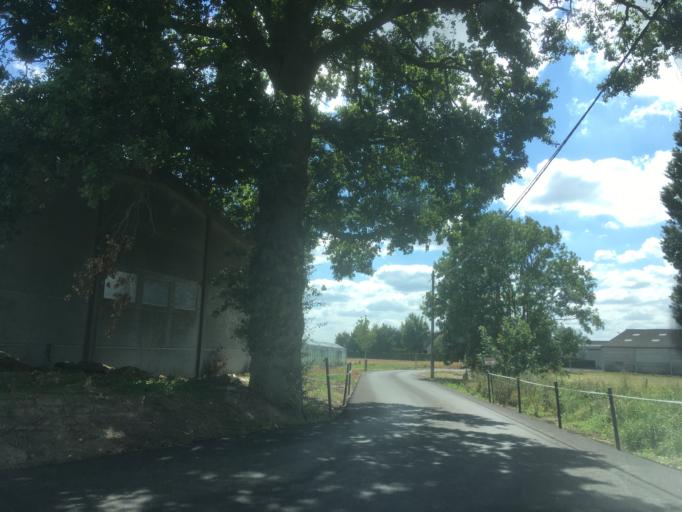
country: BE
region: Flanders
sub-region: Provincie West-Vlaanderen
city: Moorslede
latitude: 50.9281
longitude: 3.0469
